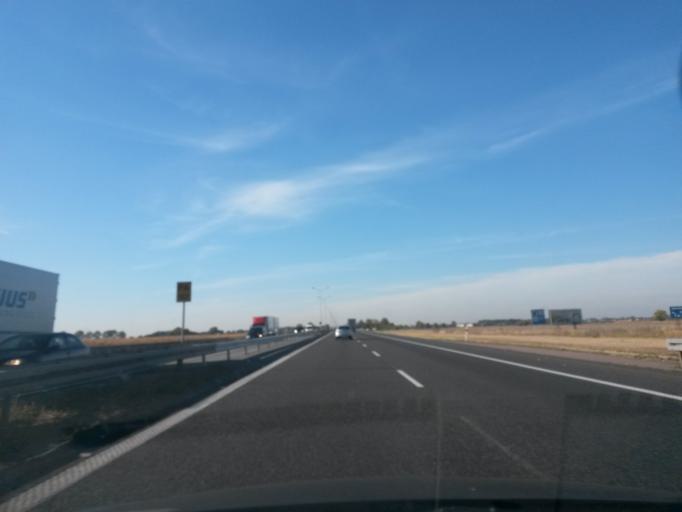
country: PL
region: Lower Silesian Voivodeship
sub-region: Powiat wroclawski
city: Zorawina
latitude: 50.9499
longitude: 17.0859
